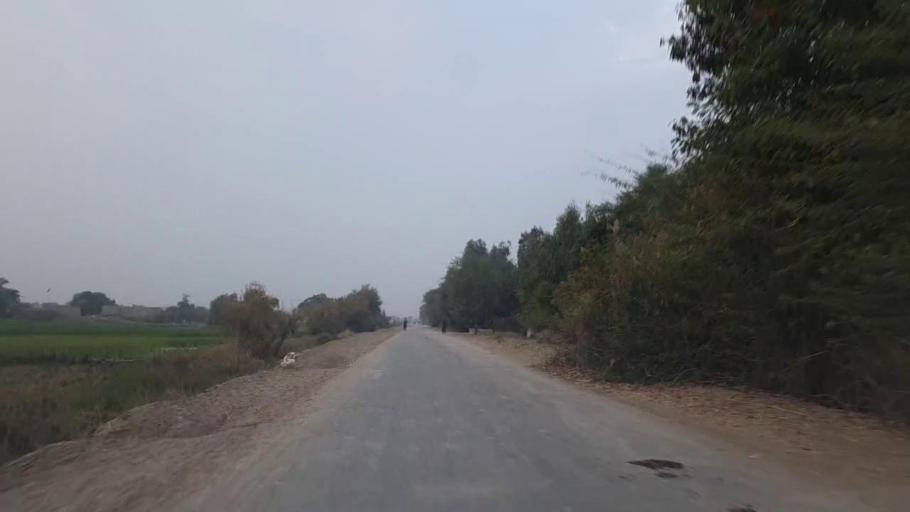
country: PK
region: Sindh
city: Jam Sahib
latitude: 26.3213
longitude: 68.5519
